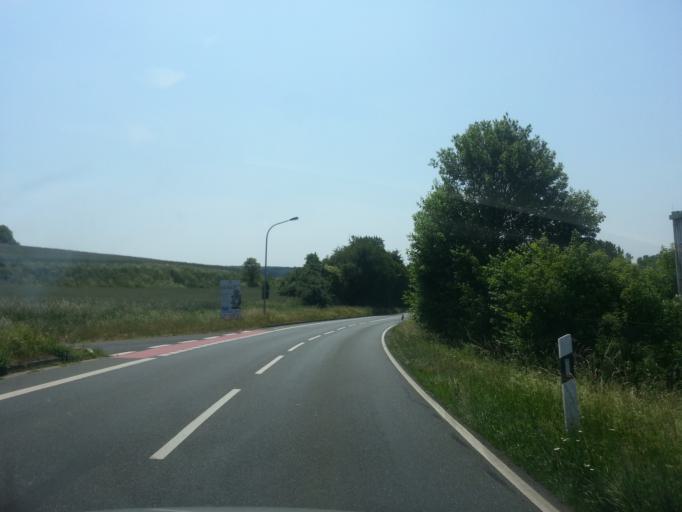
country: DE
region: Hesse
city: Ober-Ramstadt
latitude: 49.8394
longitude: 8.7451
